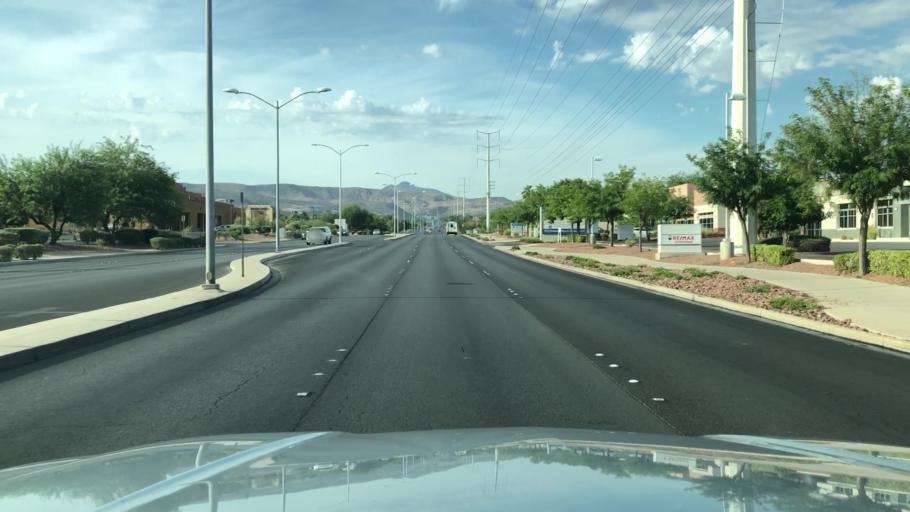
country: US
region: Nevada
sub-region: Clark County
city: Whitney
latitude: 36.0552
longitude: -115.0464
